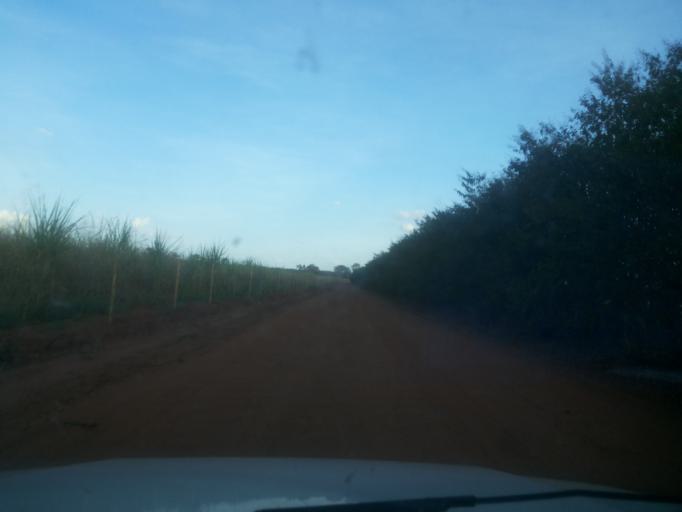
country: BR
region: Minas Gerais
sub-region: Santa Vitoria
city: Santa Vitoria
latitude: -19.0253
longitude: -50.3649
